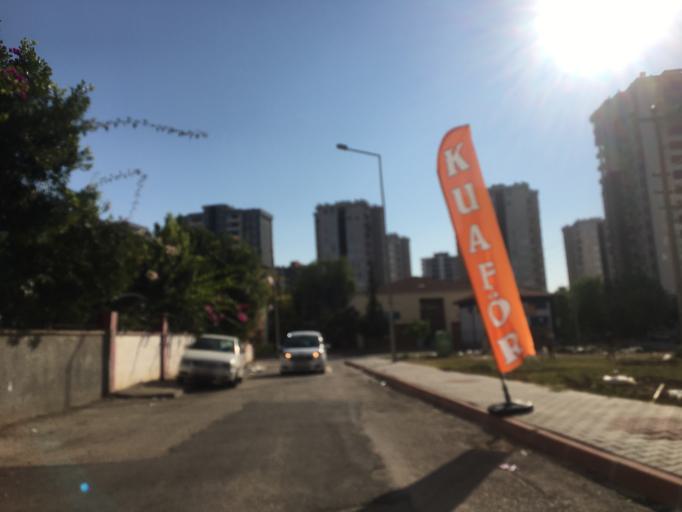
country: TR
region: Adana
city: Seyhan
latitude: 37.0278
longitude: 35.2563
